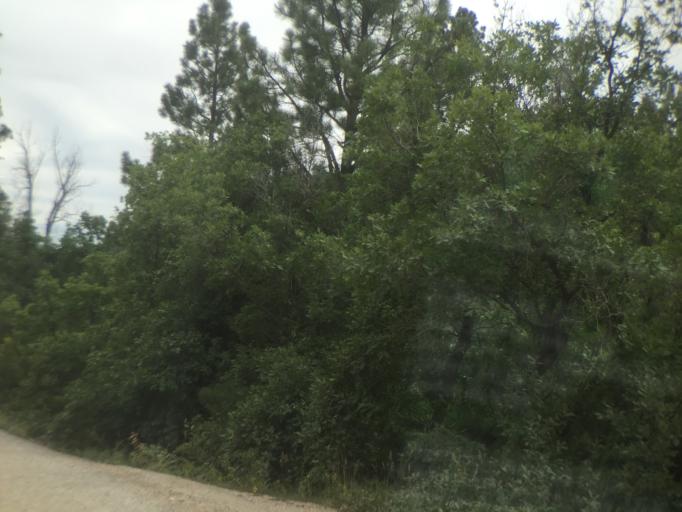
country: US
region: Colorado
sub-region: La Plata County
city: Durango
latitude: 37.3327
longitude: -107.9040
